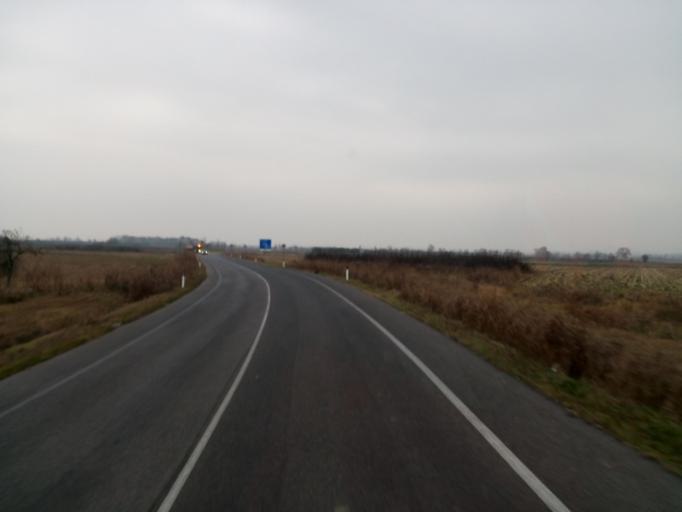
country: IT
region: Friuli Venezia Giulia
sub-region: Provincia di Udine
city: Buttrio
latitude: 46.0265
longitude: 13.3247
